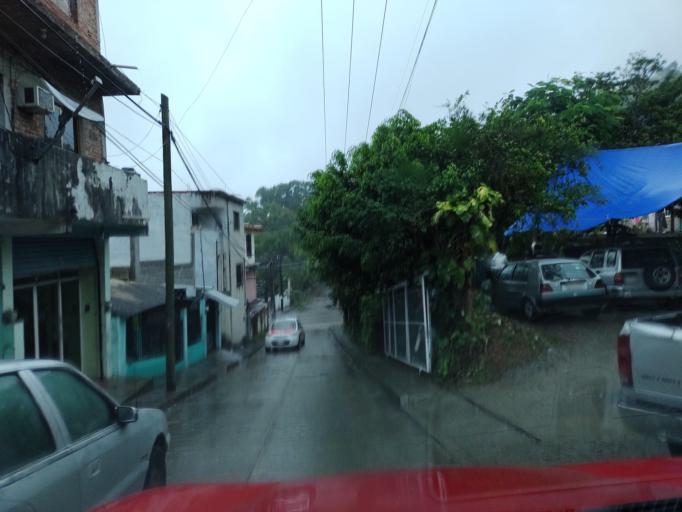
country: MX
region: Veracruz
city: Papantla de Olarte
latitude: 20.4411
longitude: -97.3353
